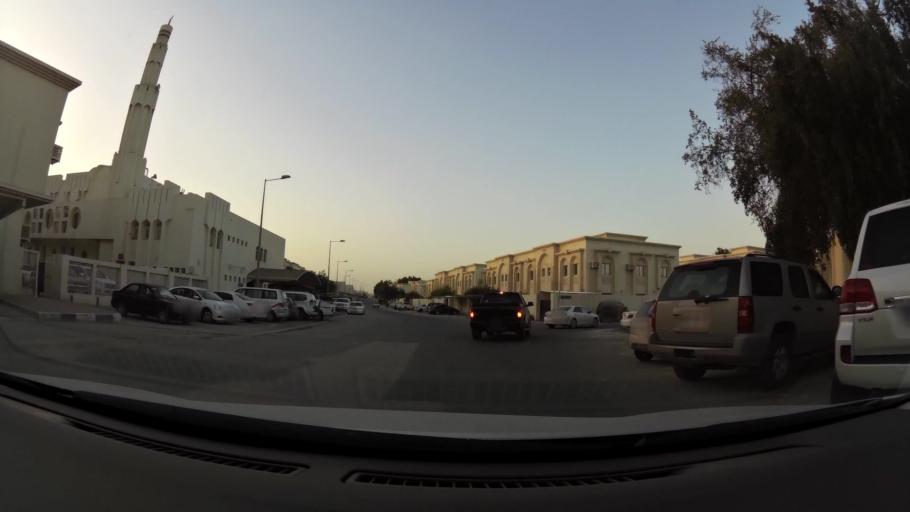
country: QA
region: Baladiyat ar Rayyan
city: Ar Rayyan
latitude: 25.3209
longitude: 51.4655
